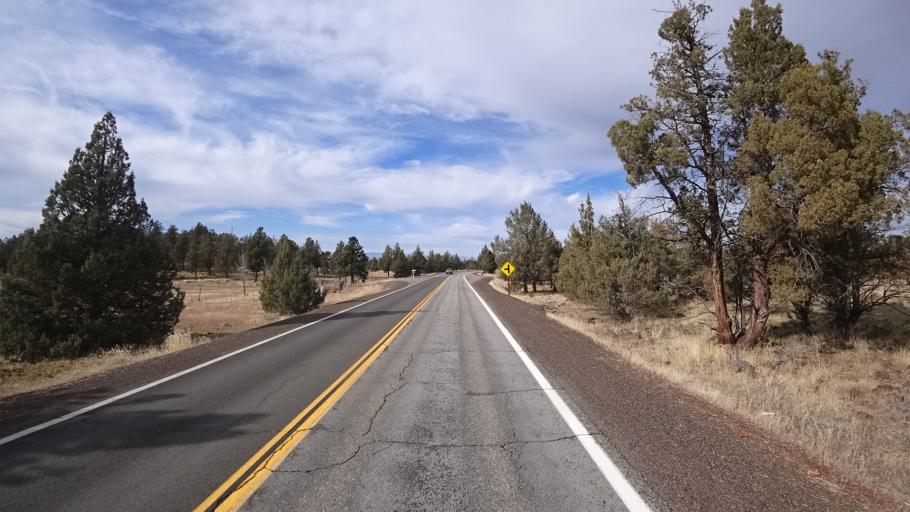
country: US
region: California
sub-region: Siskiyou County
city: Montague
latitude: 41.6076
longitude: -122.3974
